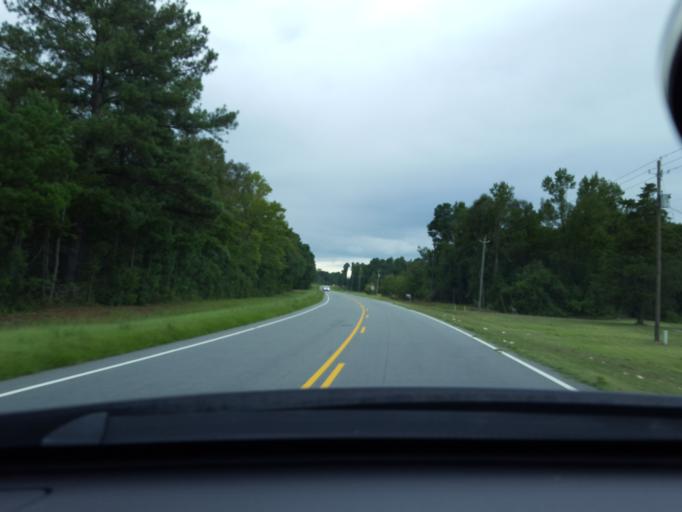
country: US
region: North Carolina
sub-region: Sampson County
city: Roseboro
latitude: 34.7561
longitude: -78.4159
